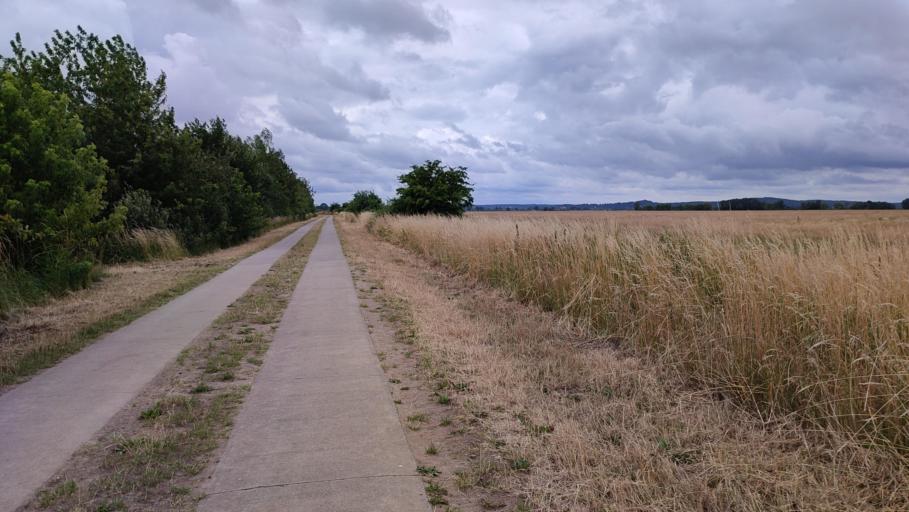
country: DE
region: Lower Saxony
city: Hitzacker
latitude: 53.1768
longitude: 11.1034
